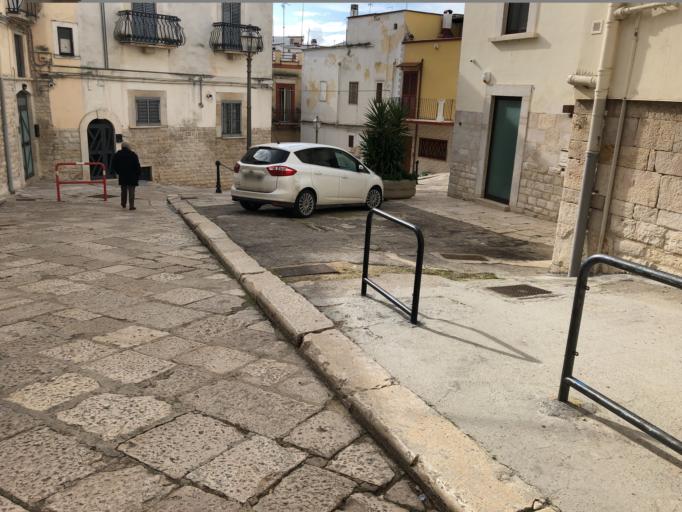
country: IT
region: Apulia
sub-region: Provincia di Barletta - Andria - Trani
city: Andria
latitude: 41.2249
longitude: 16.2949
